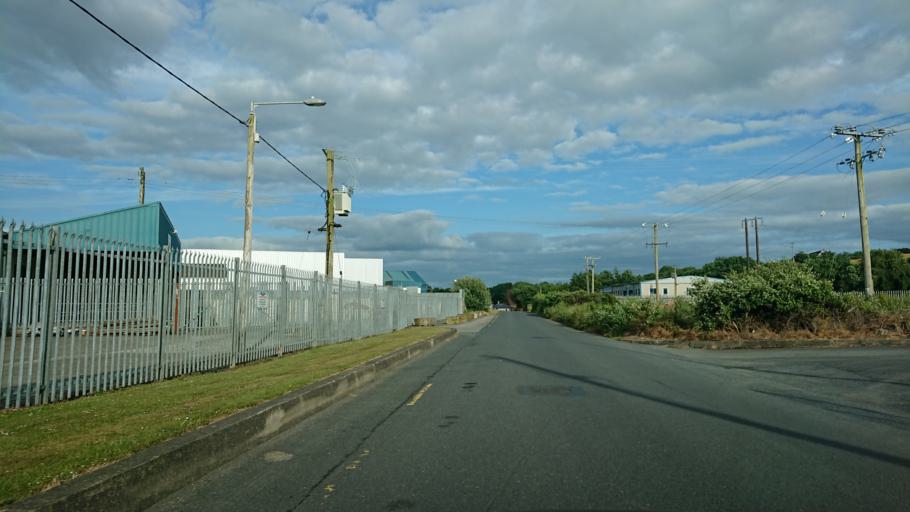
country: IE
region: Munster
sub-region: Waterford
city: Waterford
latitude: 52.2423
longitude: -7.1612
